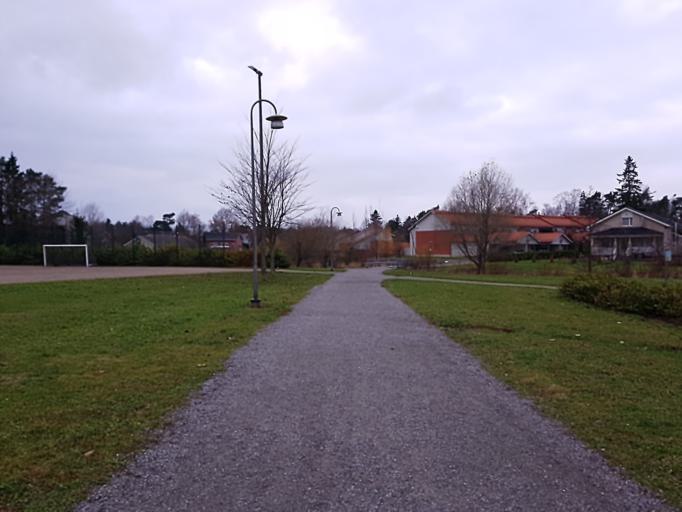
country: FI
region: Varsinais-Suomi
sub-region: Turku
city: Rusko
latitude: 60.4924
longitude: 22.2396
